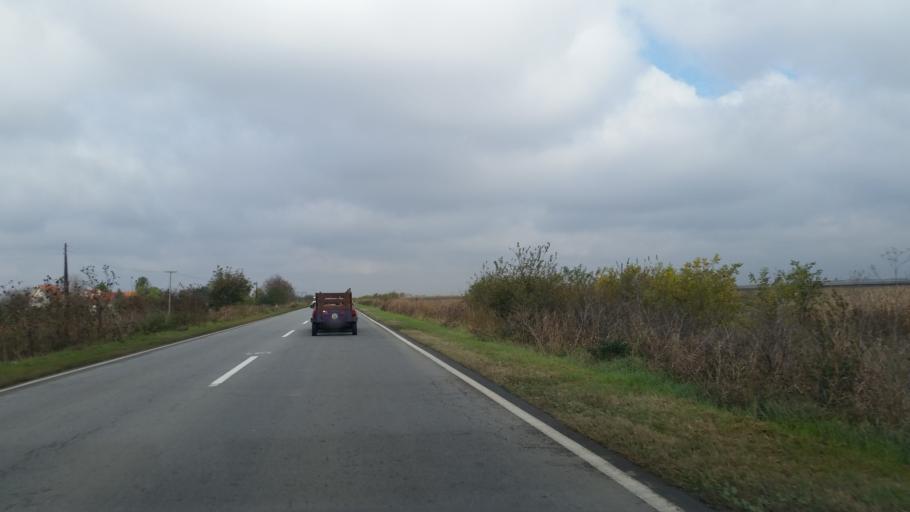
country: RS
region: Autonomna Pokrajina Vojvodina
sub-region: Srednjebanatski Okrug
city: Zrenjanin
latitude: 45.4205
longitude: 20.3714
